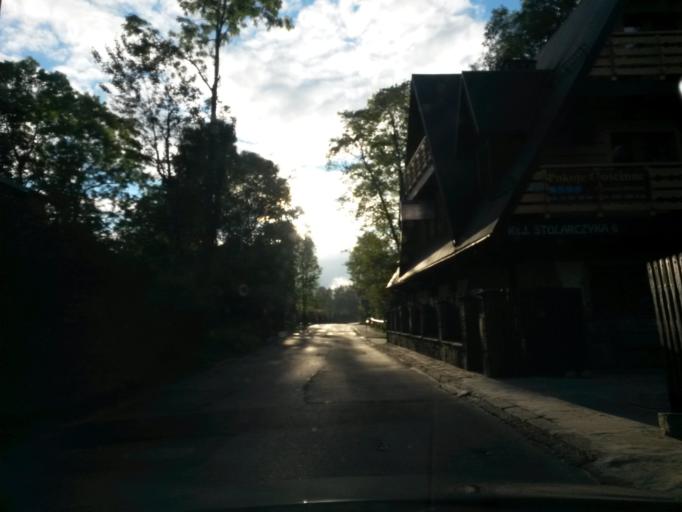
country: PL
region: Lesser Poland Voivodeship
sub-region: Powiat tatrzanski
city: Zakopane
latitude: 49.2931
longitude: 19.9475
